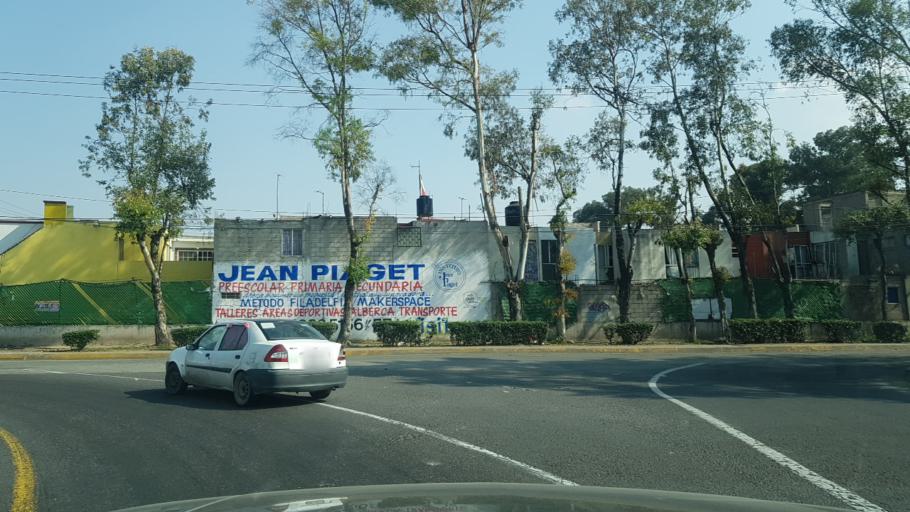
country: MX
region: Mexico
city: Santiago Teyahualco
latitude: 19.6635
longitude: -99.1367
